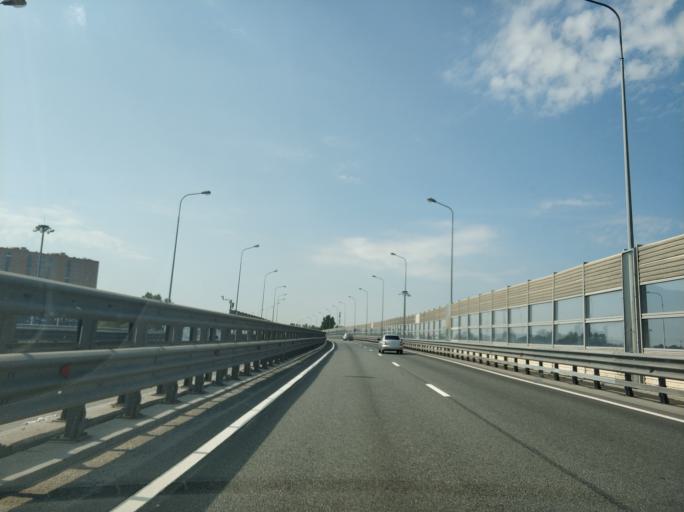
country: RU
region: St.-Petersburg
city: Krasnogvargeisky
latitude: 59.9827
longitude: 30.5106
